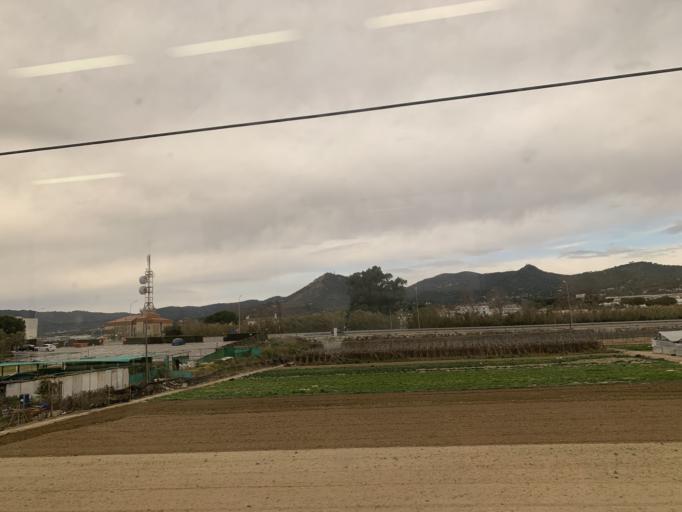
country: ES
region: Catalonia
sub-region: Provincia de Barcelona
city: Cabrera de Mar
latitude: 41.5110
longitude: 2.4095
